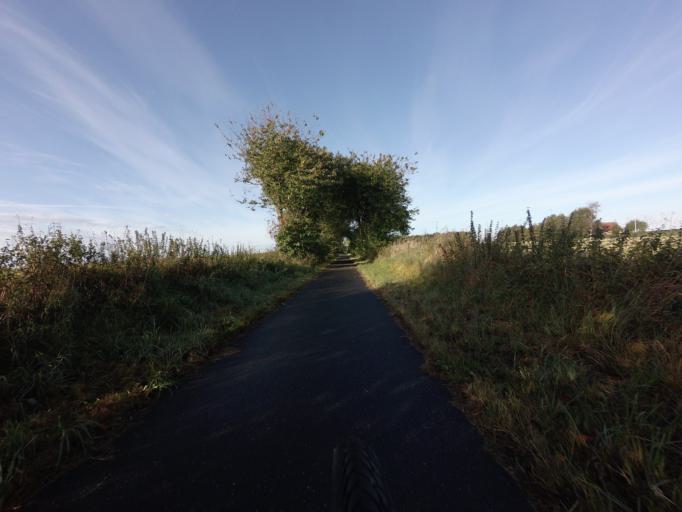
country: DK
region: Central Jutland
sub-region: Viborg Kommune
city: Bjerringbro
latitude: 56.4914
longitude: 9.6518
